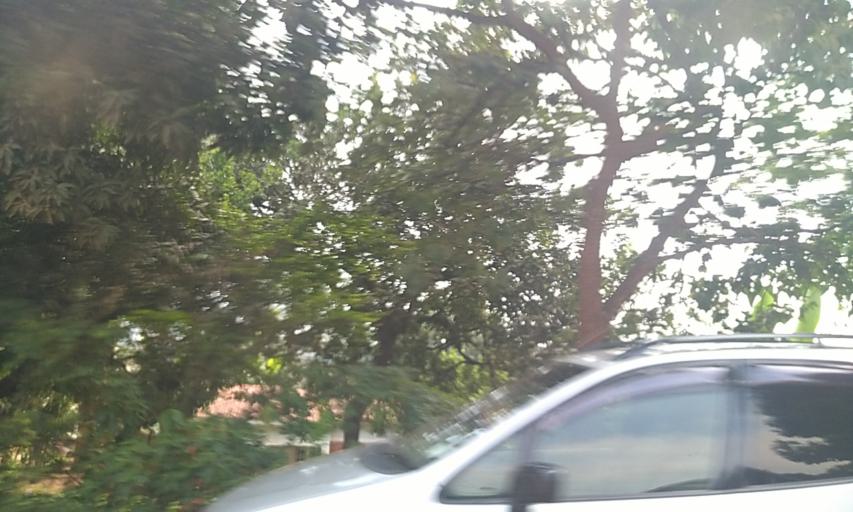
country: UG
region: Central Region
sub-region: Kampala District
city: Kampala
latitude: 0.3019
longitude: 32.5587
